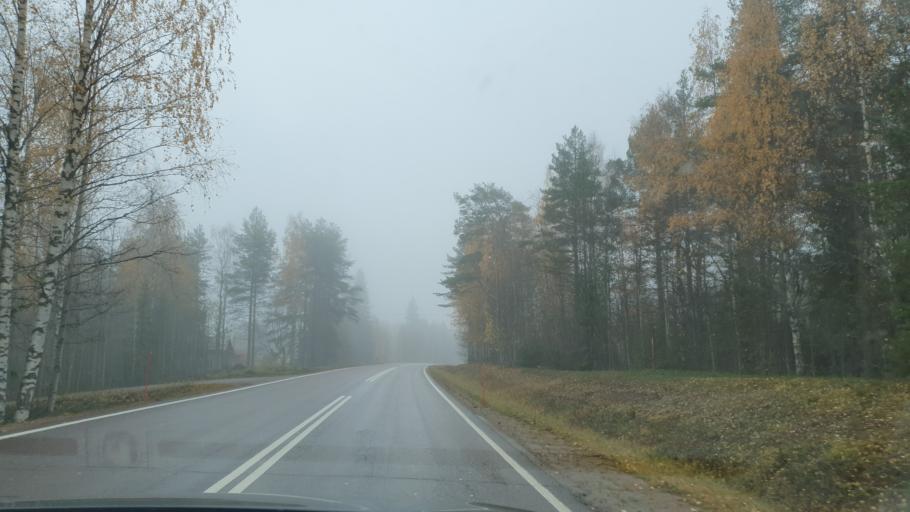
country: FI
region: Lapland
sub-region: Rovaniemi
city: Rovaniemi
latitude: 66.8107
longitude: 25.4064
